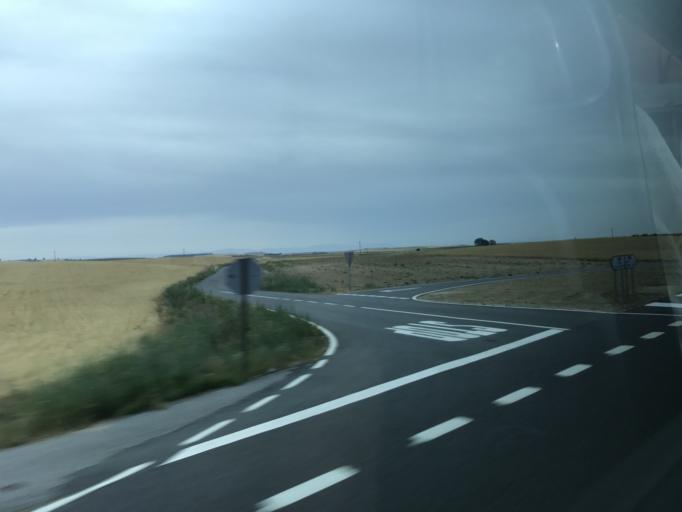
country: ES
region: Castille and Leon
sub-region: Provincia de Segovia
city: Rapariegos
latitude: 41.0911
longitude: -4.6378
